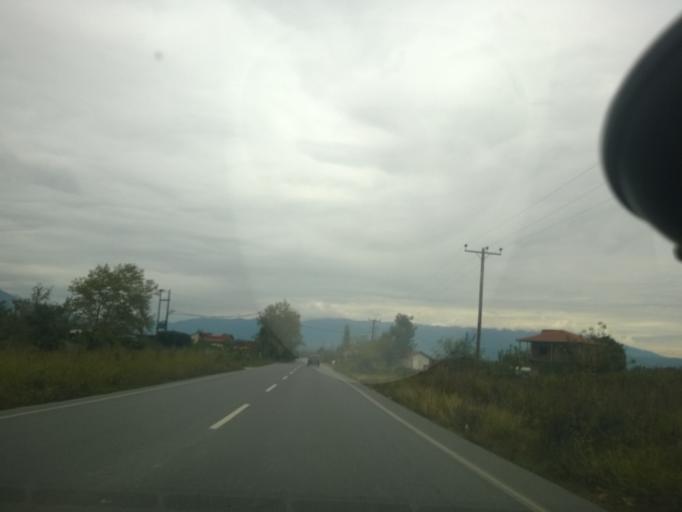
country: GR
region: Central Macedonia
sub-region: Nomos Pellis
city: Loutraki
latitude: 40.9711
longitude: 21.9567
